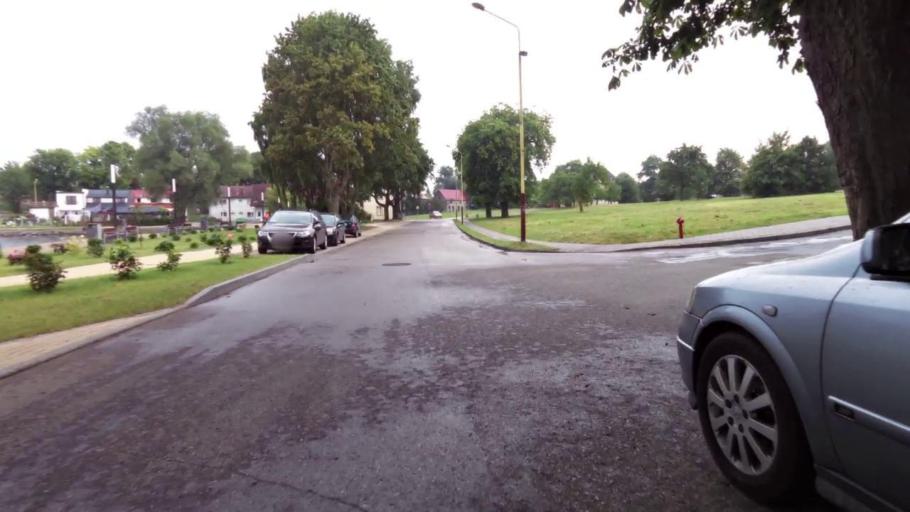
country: PL
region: West Pomeranian Voivodeship
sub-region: Powiat stargardzki
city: Insko
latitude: 53.4383
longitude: 15.5475
